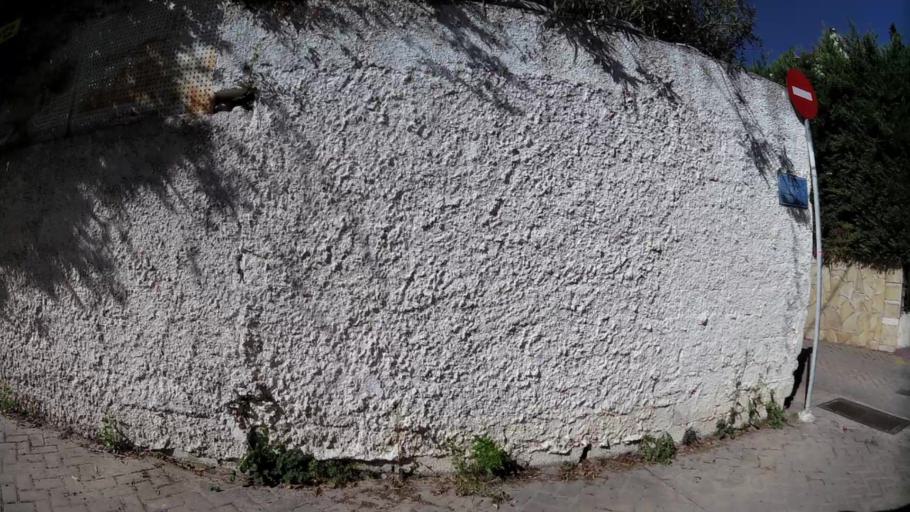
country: GR
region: Attica
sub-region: Nomarchia Athinas
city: Kifisia
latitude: 38.0814
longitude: 23.7968
